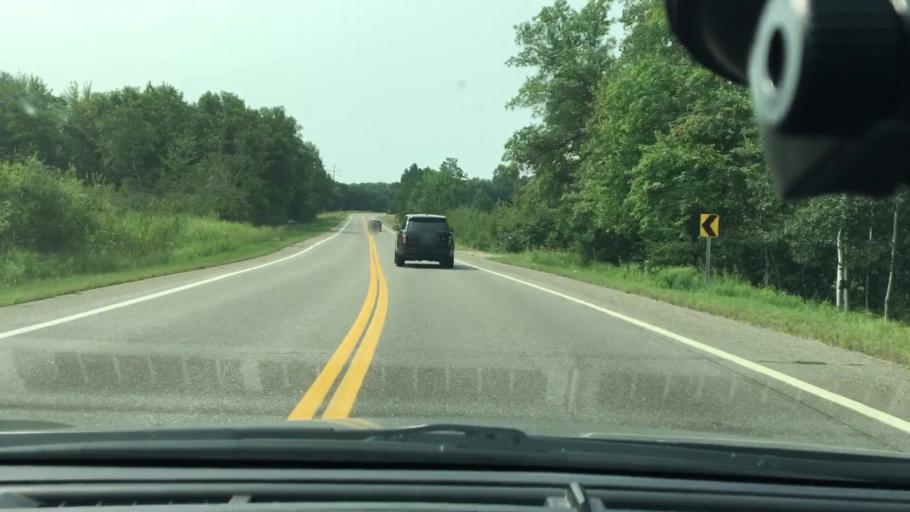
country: US
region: Minnesota
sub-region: Cass County
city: East Gull Lake
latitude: 46.3821
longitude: -94.3316
